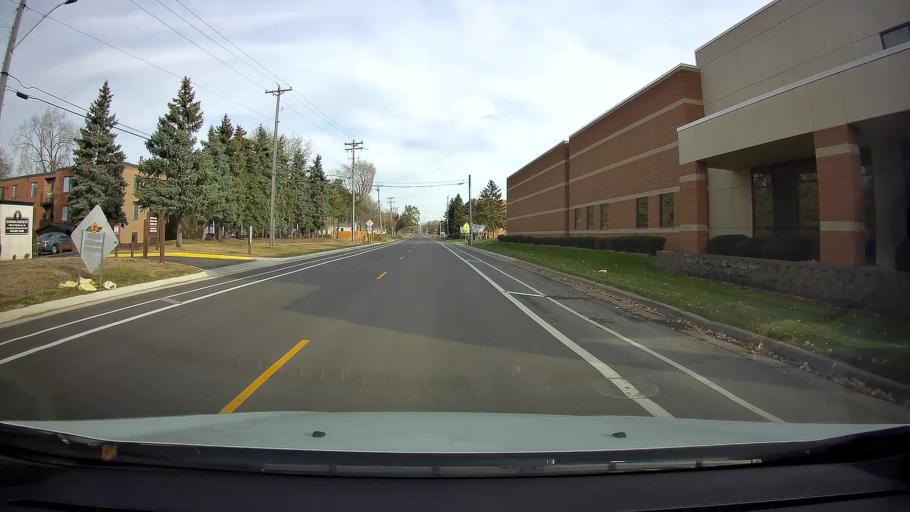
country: US
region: Minnesota
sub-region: Ramsey County
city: Lauderdale
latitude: 44.9843
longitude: -93.2273
